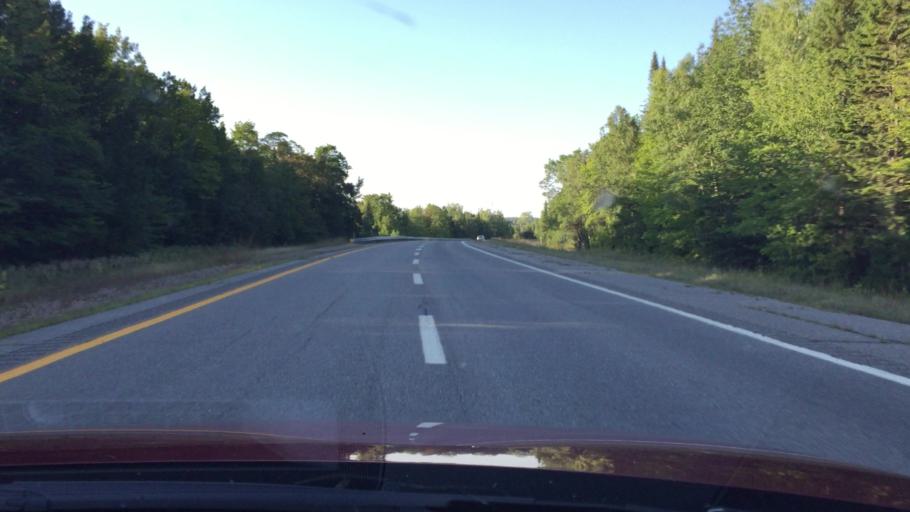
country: US
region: Maine
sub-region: Penobscot County
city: Patten
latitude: 45.8364
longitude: -68.4330
